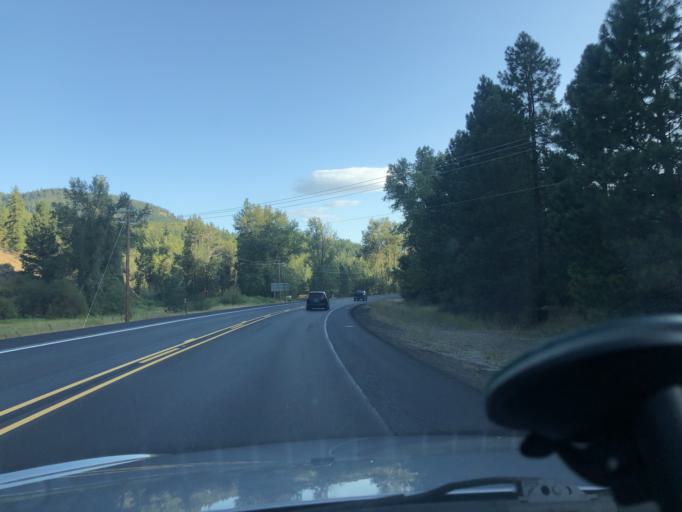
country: US
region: Washington
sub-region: Kittitas County
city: Cle Elum
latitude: 47.2106
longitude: -120.6983
